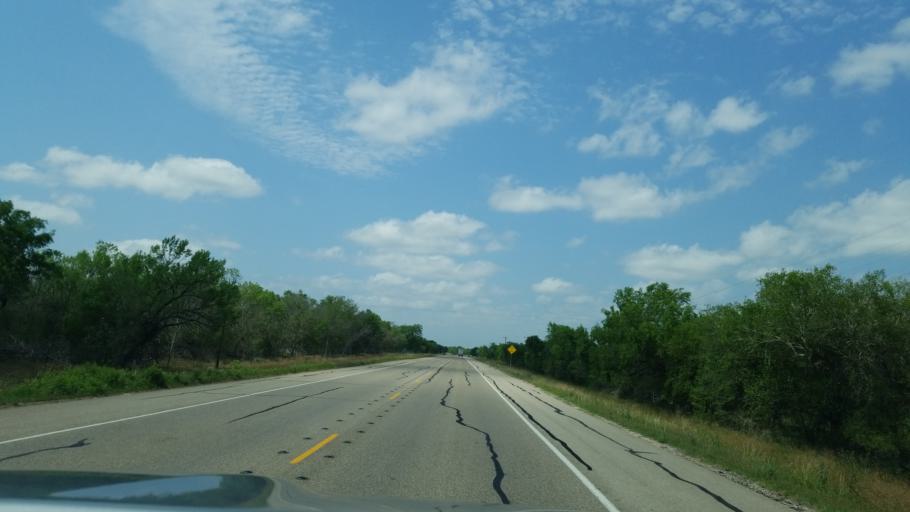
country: US
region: Texas
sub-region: Frio County
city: Pearsall
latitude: 28.9952
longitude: -99.2243
